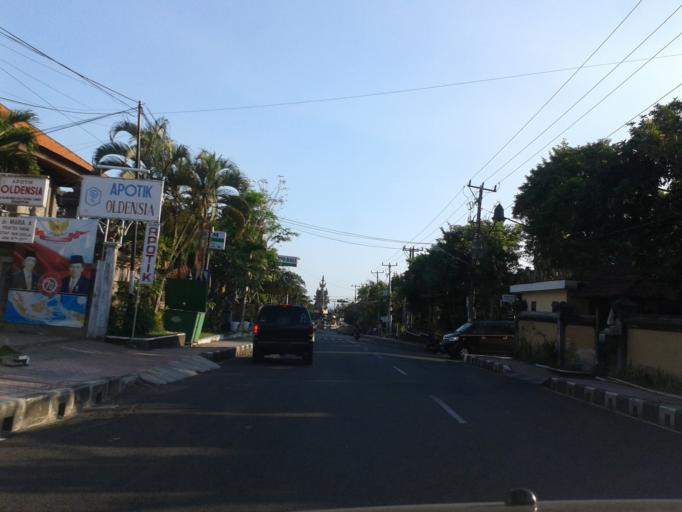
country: ID
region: Bali
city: Semarapura
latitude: -8.5336
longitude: 115.4039
